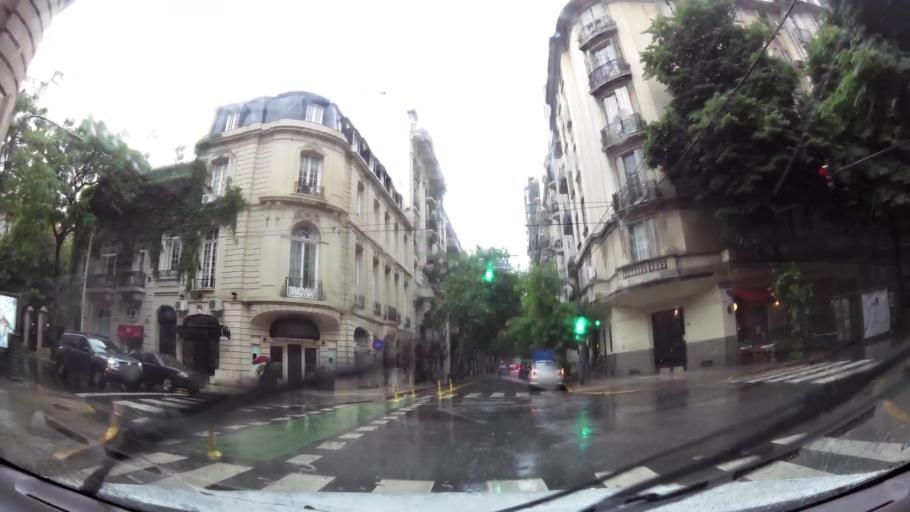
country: AR
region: Buenos Aires F.D.
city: Retiro
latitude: -34.5906
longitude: -58.3870
